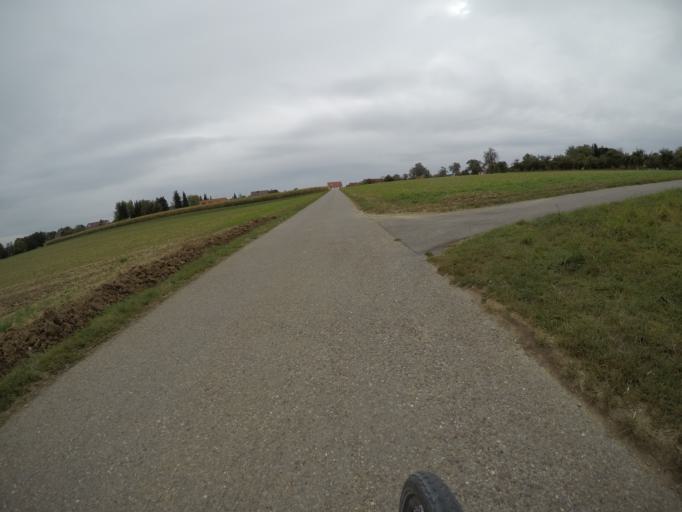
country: DE
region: Baden-Wuerttemberg
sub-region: Regierungsbezirk Stuttgart
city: Eberdingen
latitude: 48.8556
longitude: 8.9871
